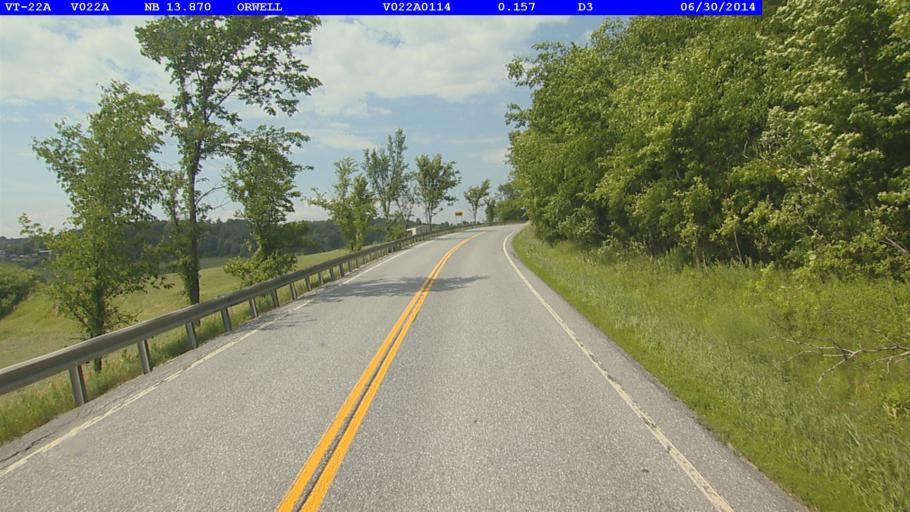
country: US
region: New York
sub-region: Essex County
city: Ticonderoga
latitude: 43.7596
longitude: -73.3122
